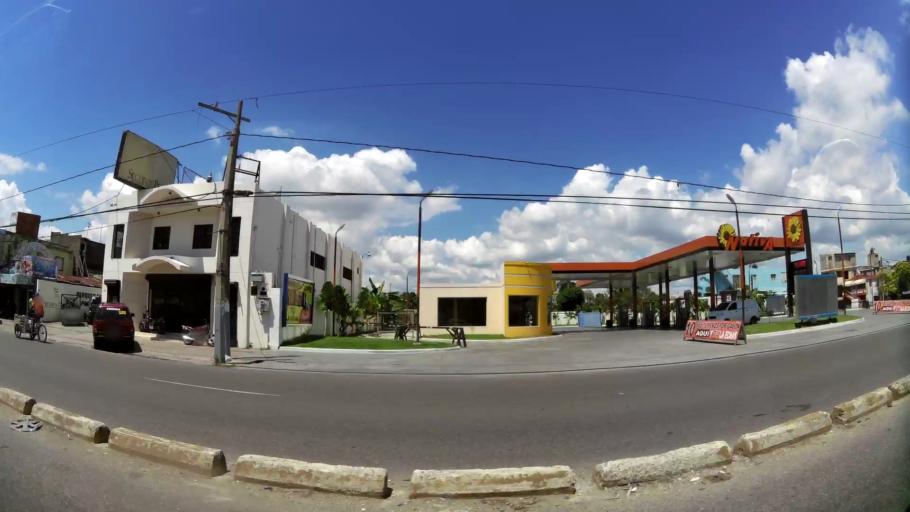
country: DO
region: Nacional
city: Ensanche Luperon
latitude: 18.4976
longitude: -69.8933
